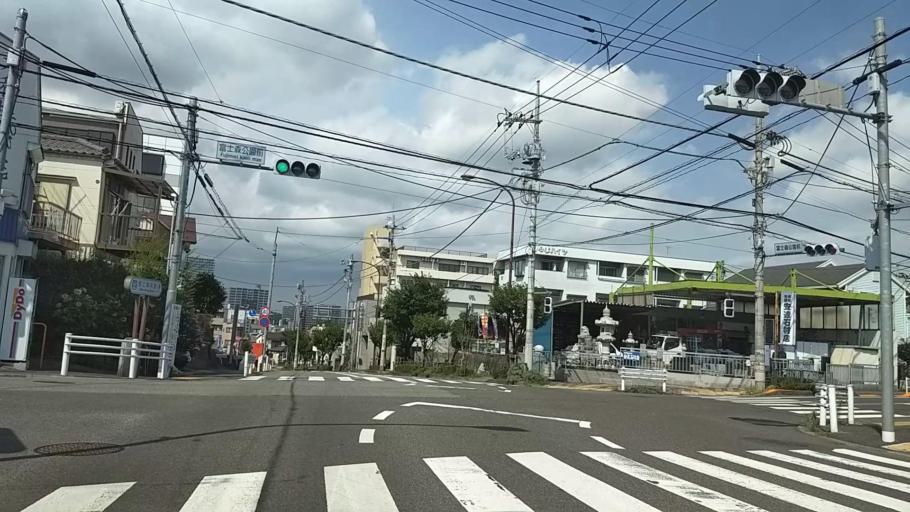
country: JP
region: Tokyo
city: Hachioji
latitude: 35.6525
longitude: 139.3267
